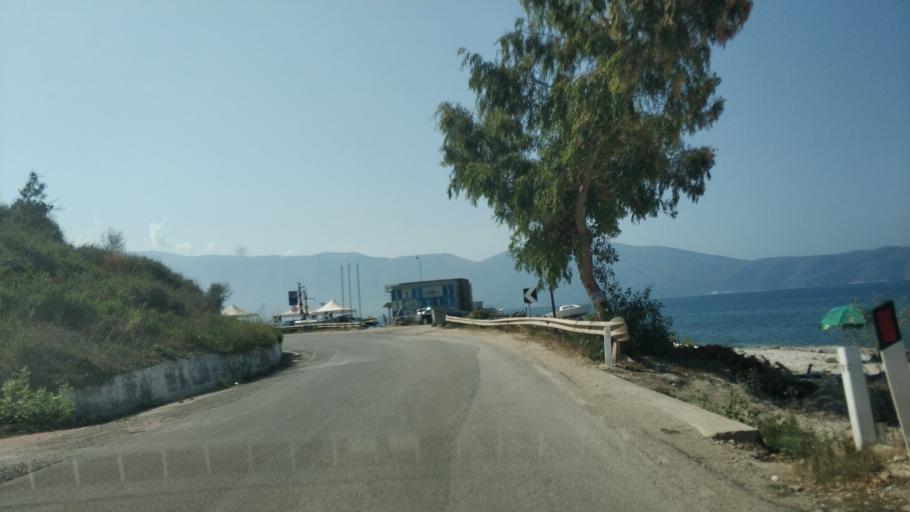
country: AL
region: Vlore
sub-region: Rrethi i Vlores
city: Orikum
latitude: 40.3624
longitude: 19.4801
